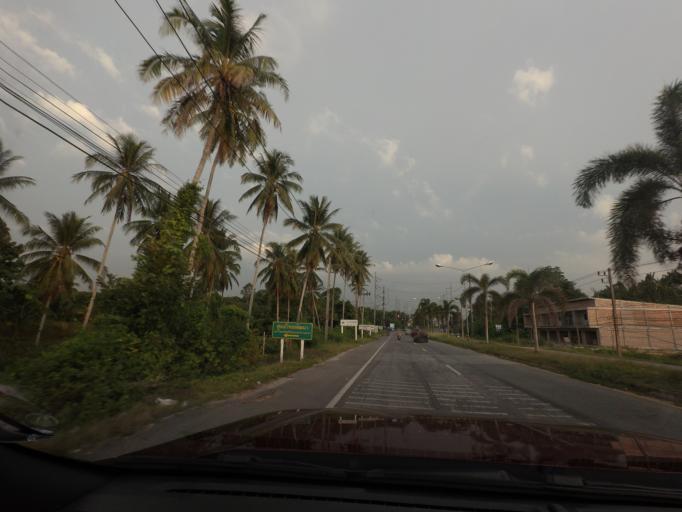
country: TH
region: Yala
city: Yala
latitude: 6.5760
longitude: 101.1991
